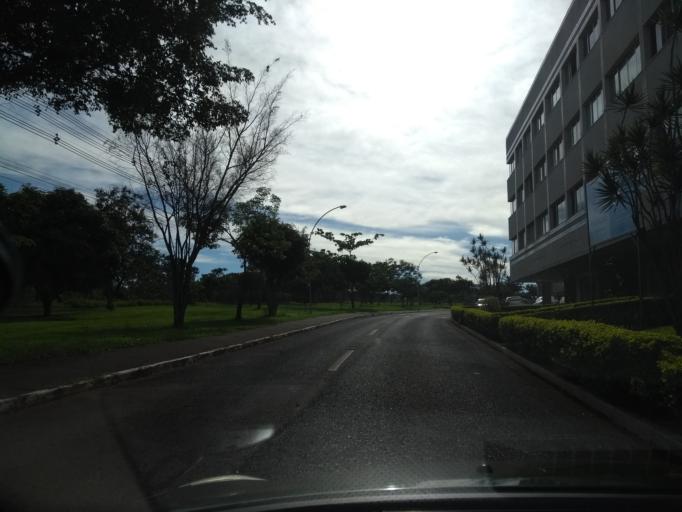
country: BR
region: Federal District
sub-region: Brasilia
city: Brasilia
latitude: -15.7829
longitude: -47.9280
